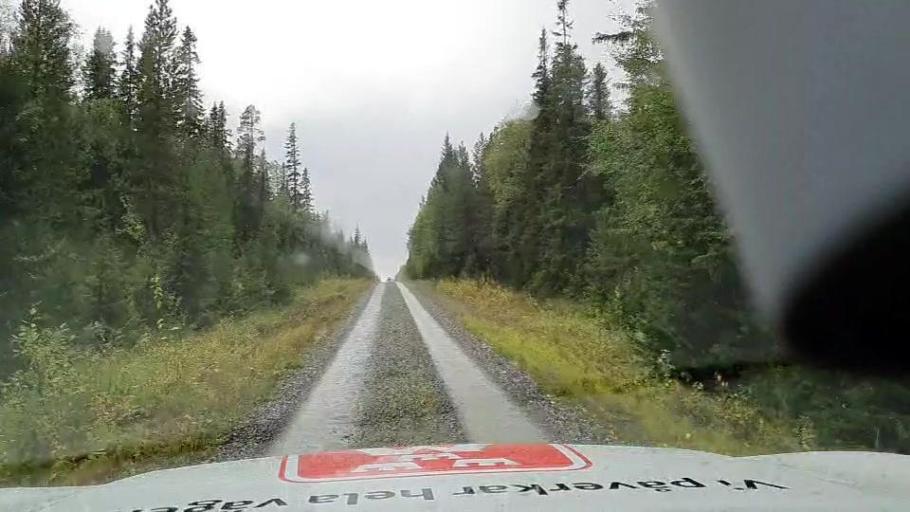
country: SE
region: Jaemtland
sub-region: Are Kommun
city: Jarpen
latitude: 63.2055
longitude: 13.2875
